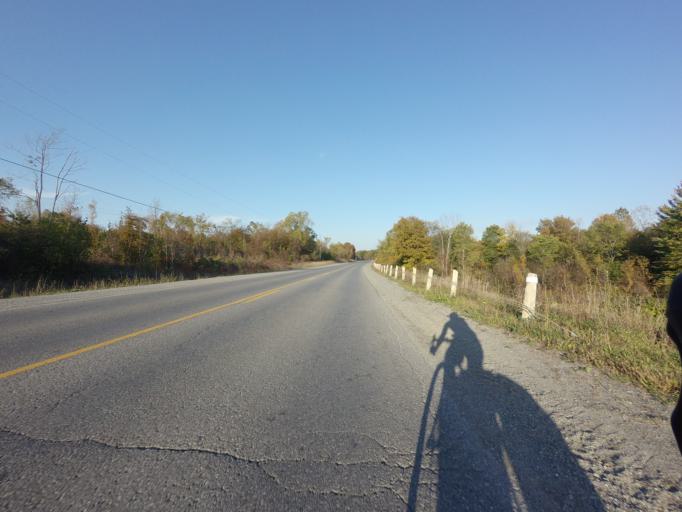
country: CA
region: Ontario
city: Kingston
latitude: 44.3576
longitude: -76.4285
